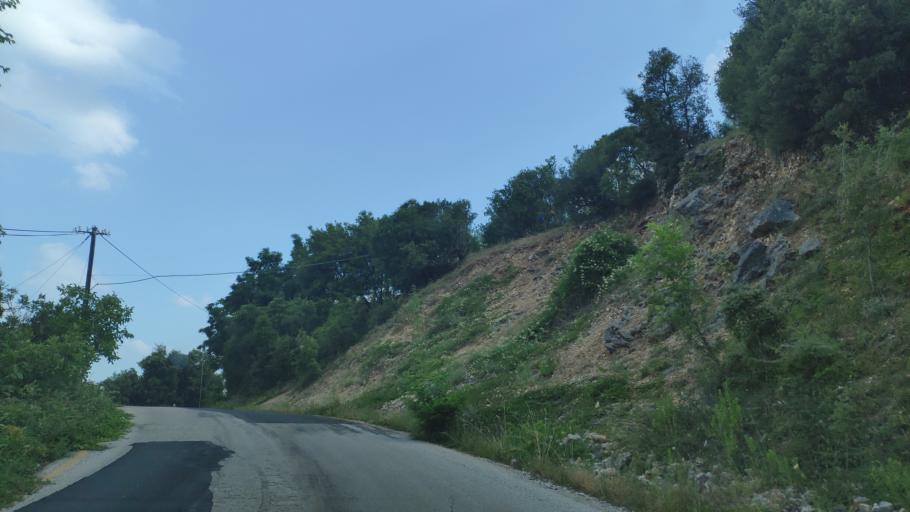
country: GR
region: Epirus
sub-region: Nomos Artas
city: Agios Dimitrios
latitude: 39.3740
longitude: 21.0248
